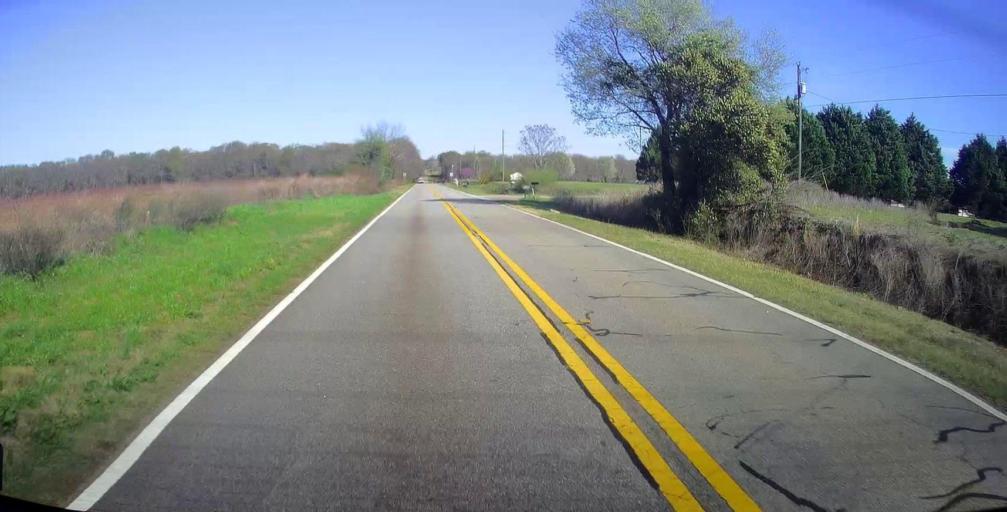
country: US
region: Georgia
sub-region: Peach County
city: Byron
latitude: 32.6446
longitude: -83.8005
